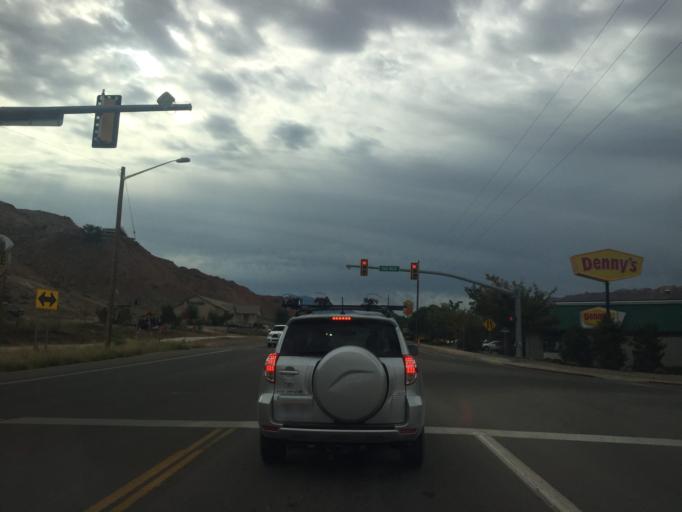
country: US
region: Utah
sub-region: Grand County
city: Moab
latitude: 38.5889
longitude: -109.5611
